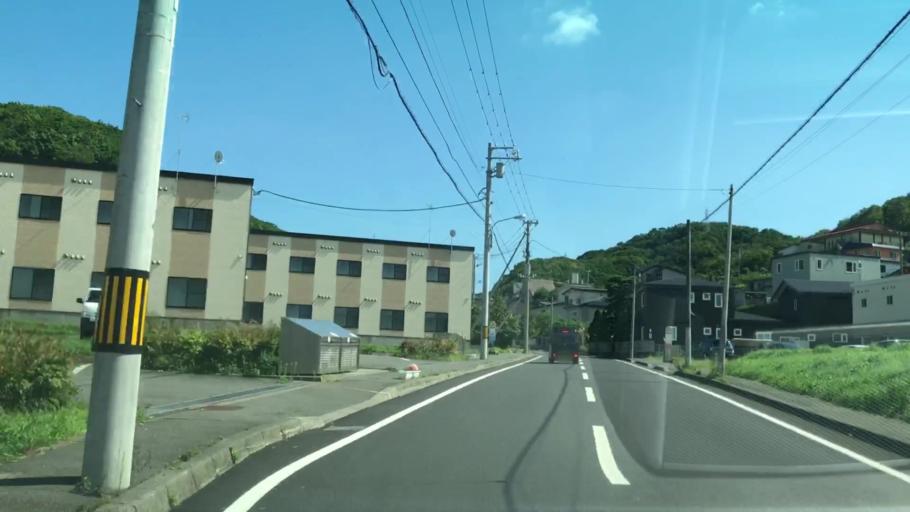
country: JP
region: Hokkaido
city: Muroran
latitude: 42.3096
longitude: 140.9981
